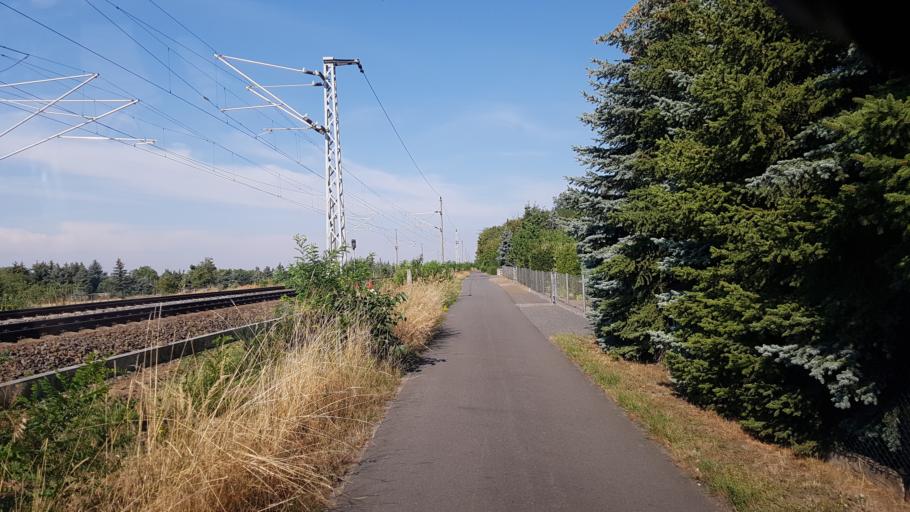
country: DE
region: Brandenburg
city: Plessa
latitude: 51.4708
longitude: 13.6025
